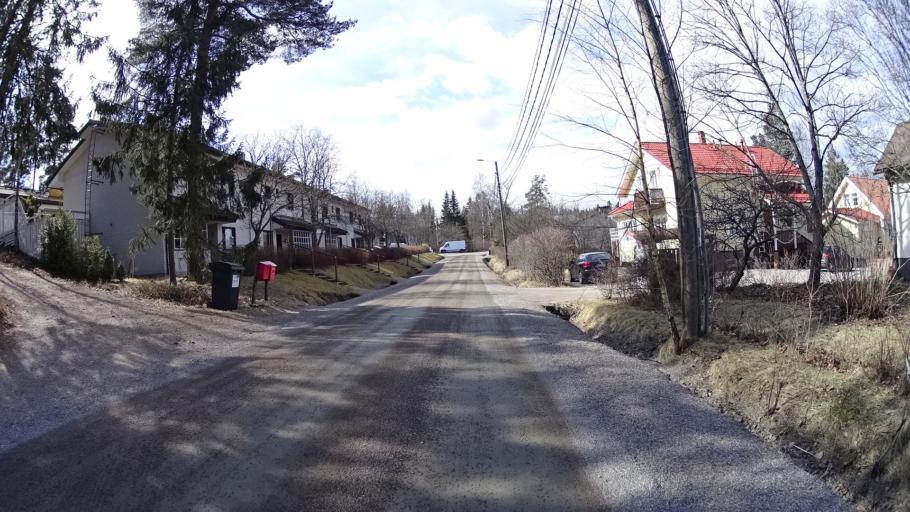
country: FI
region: Uusimaa
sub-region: Helsinki
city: Kilo
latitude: 60.2117
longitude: 24.7581
